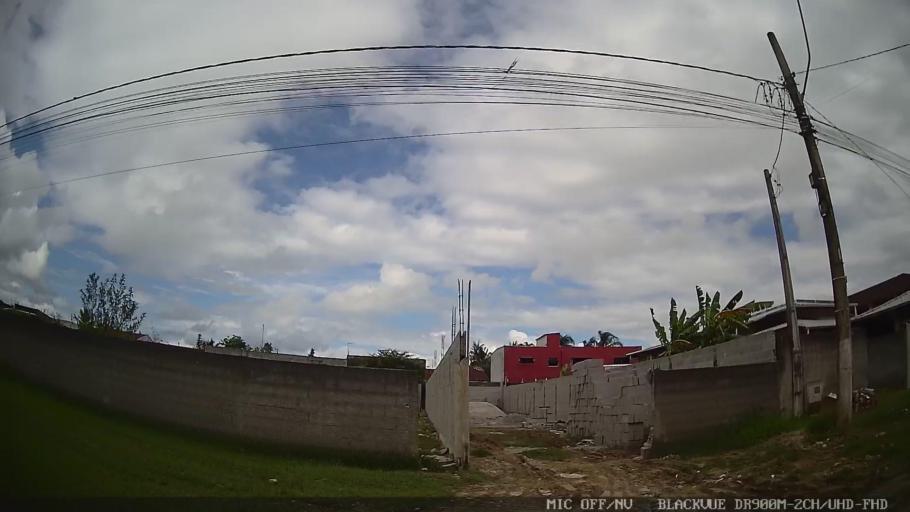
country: BR
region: Sao Paulo
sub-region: Caraguatatuba
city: Caraguatatuba
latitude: -23.6383
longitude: -45.4431
